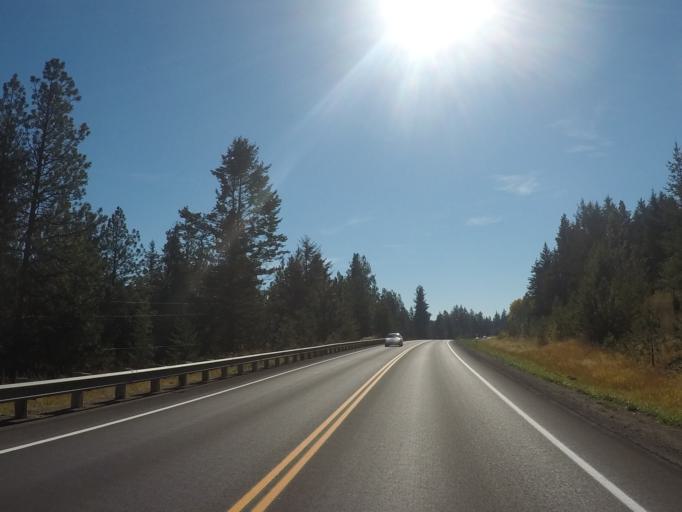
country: US
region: Montana
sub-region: Lake County
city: Polson
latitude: 47.7994
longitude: -114.2363
